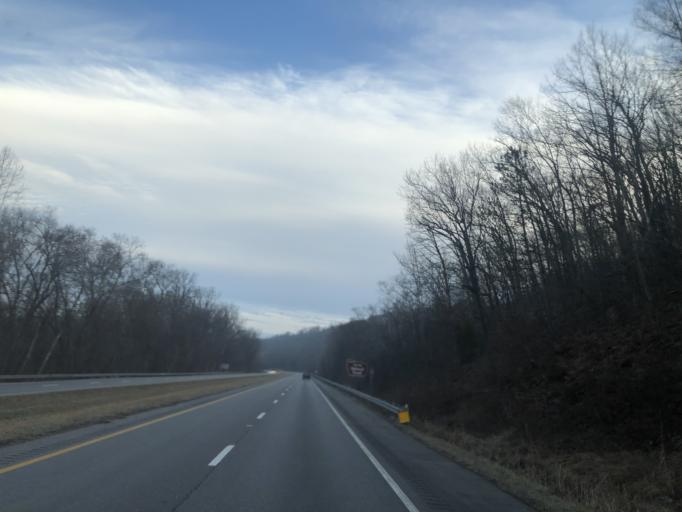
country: US
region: Ohio
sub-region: Athens County
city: Chauncey
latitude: 39.3941
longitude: -82.1618
